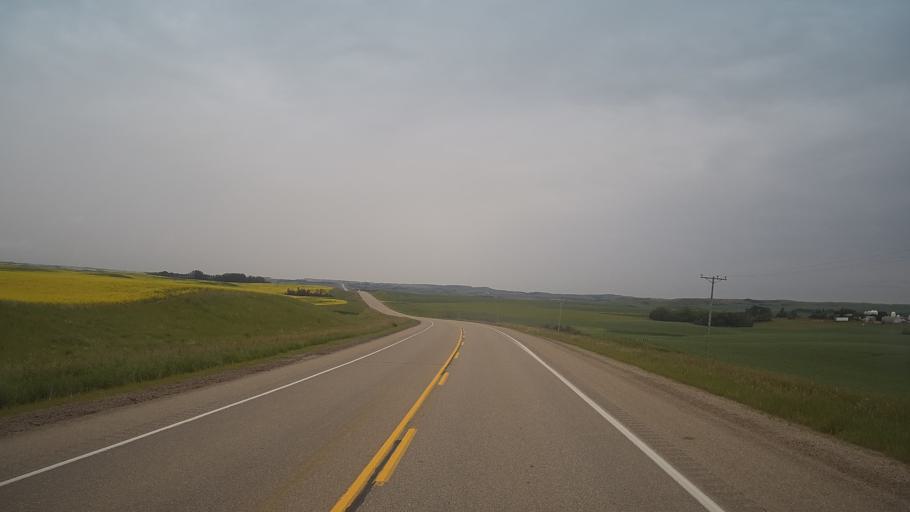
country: CA
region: Saskatchewan
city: Biggar
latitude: 52.0561
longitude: -107.7783
